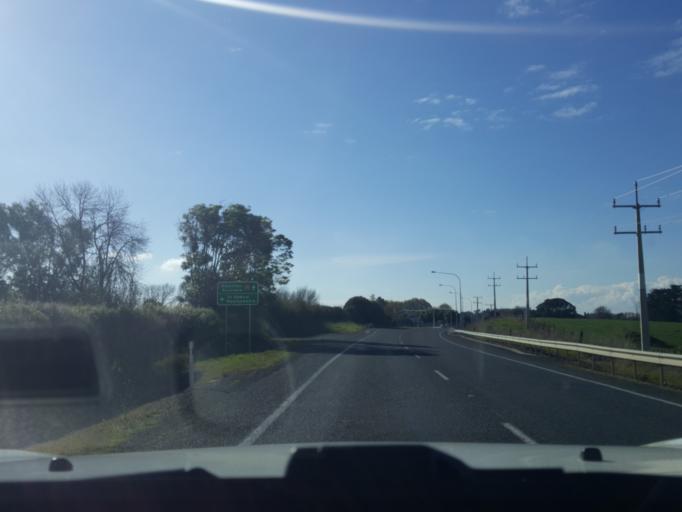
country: NZ
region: Waikato
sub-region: Waikato District
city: Ngaruawahia
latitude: -37.7564
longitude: 175.1520
